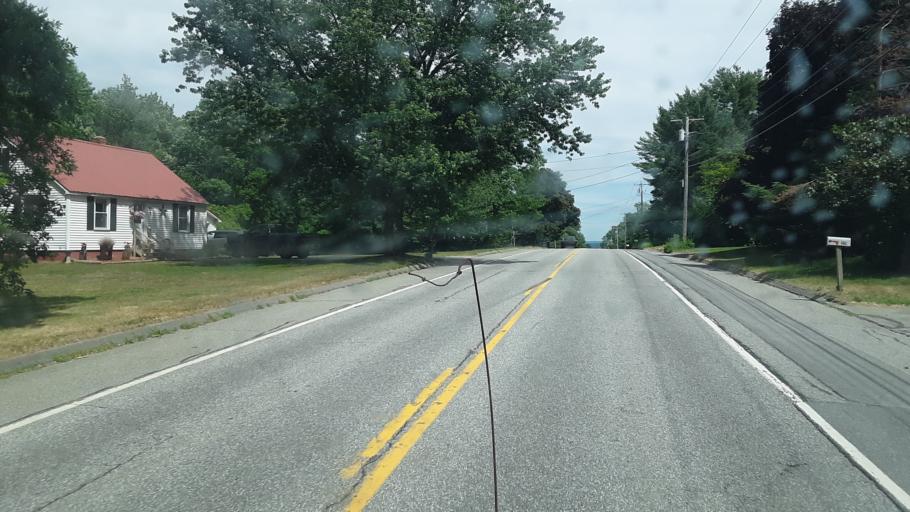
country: US
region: Maine
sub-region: Somerset County
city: Fairfield
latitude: 44.5980
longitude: -69.6414
